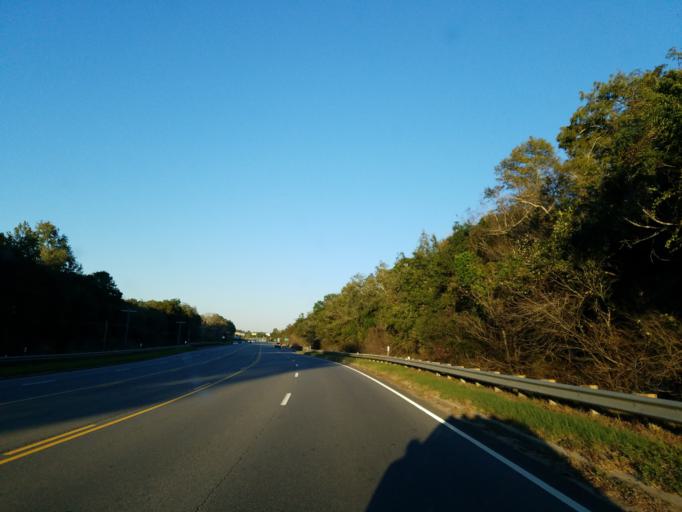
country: US
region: Georgia
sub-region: Tift County
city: Unionville
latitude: 31.4380
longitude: -83.5628
